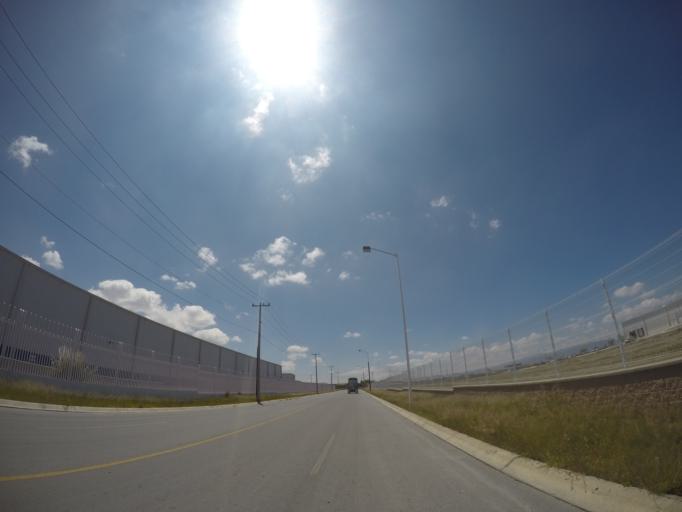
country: MX
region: San Luis Potosi
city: La Pila
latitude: 21.9701
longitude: -100.8741
